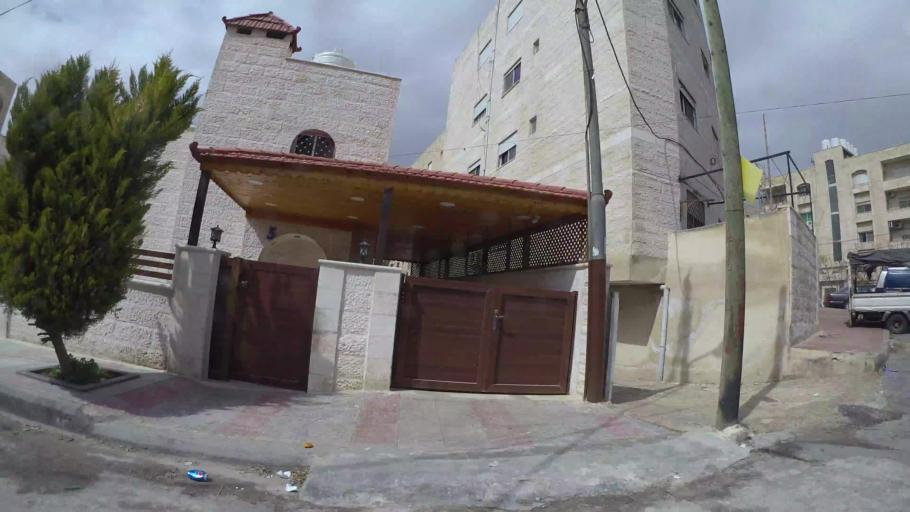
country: JO
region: Amman
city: Amman
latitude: 31.9877
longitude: 35.9217
